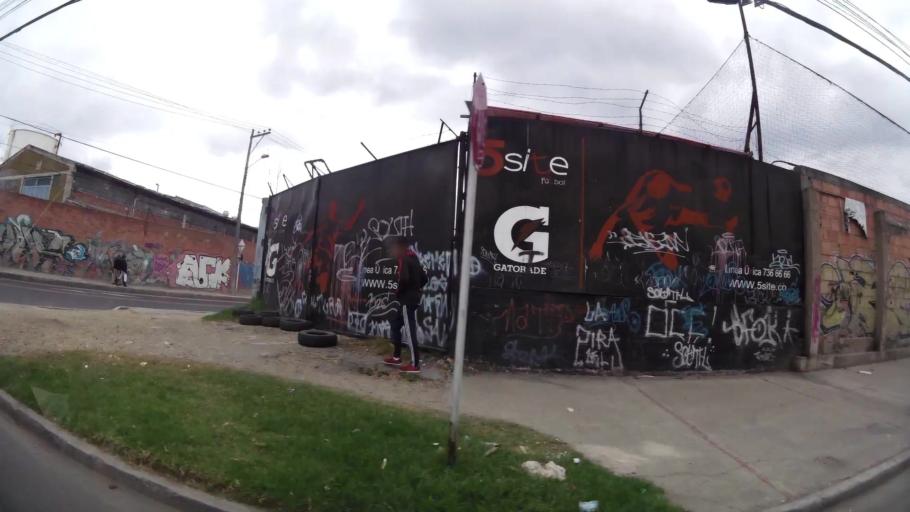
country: CO
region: Bogota D.C.
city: Bogota
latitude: 4.6023
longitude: -74.1347
